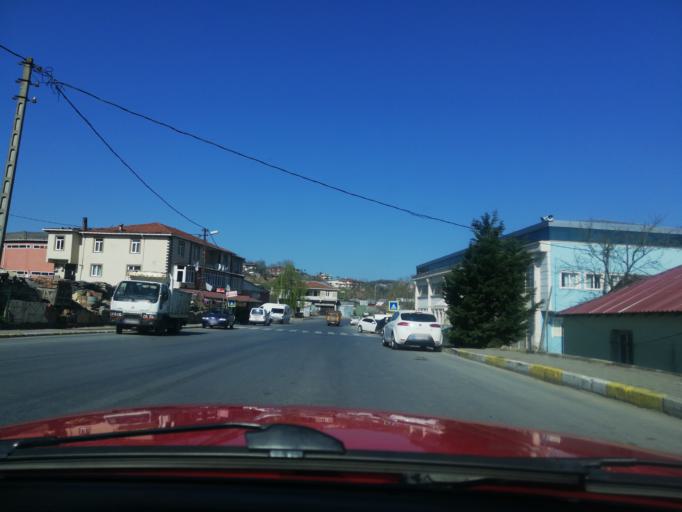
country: TR
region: Istanbul
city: Mahmut Sevket Pasa
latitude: 41.0940
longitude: 29.1436
